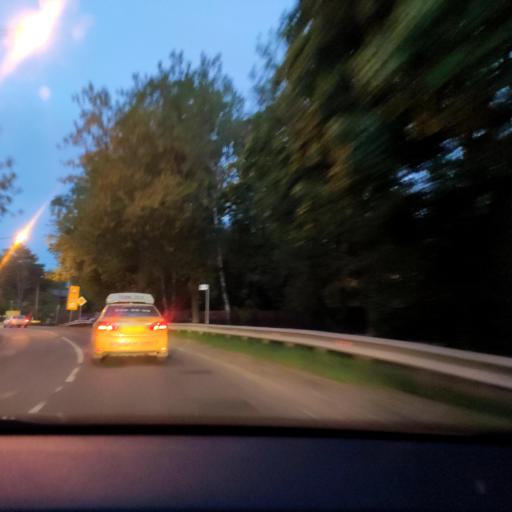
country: RU
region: Moskovskaya
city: Yubileyny
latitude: 55.9454
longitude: 37.8370
